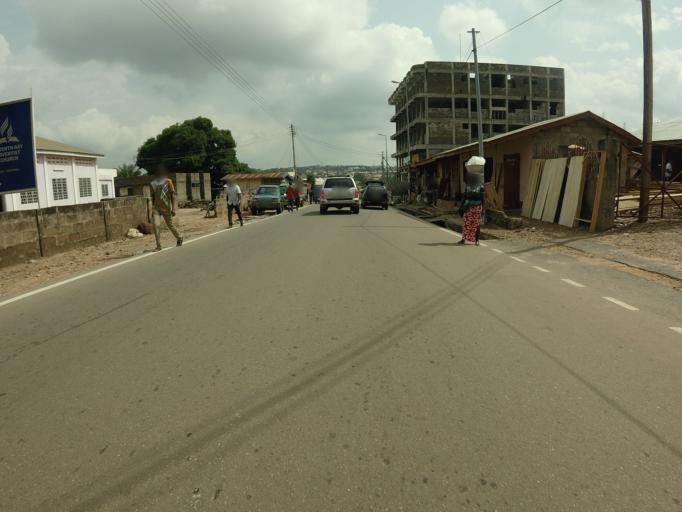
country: GH
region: Volta
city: Ho
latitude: 6.6179
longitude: 0.4732
